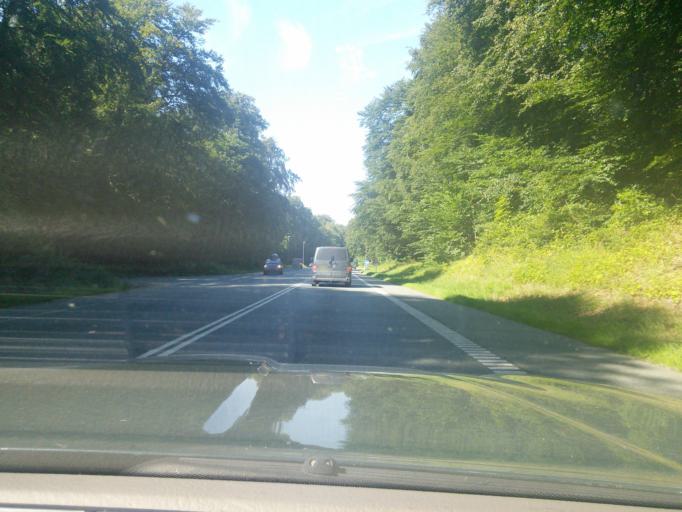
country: DK
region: Capital Region
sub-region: Halsnaes Kommune
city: Frederiksvaerk
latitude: 55.9724
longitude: 12.0302
